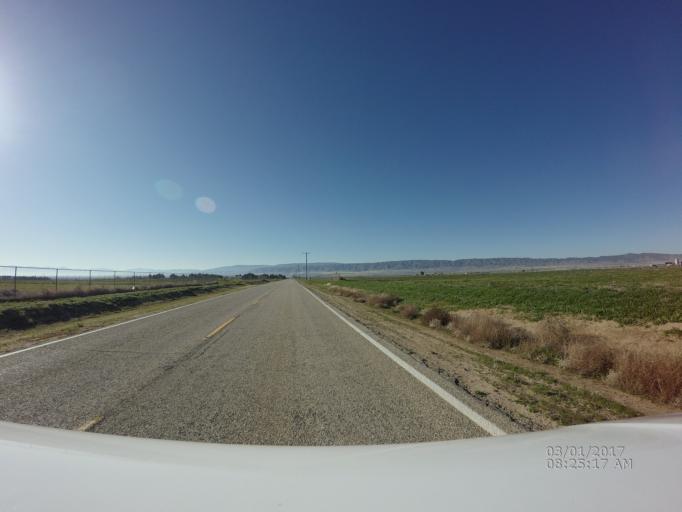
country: US
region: California
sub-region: Los Angeles County
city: Quartz Hill
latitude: 34.7136
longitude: -118.2544
